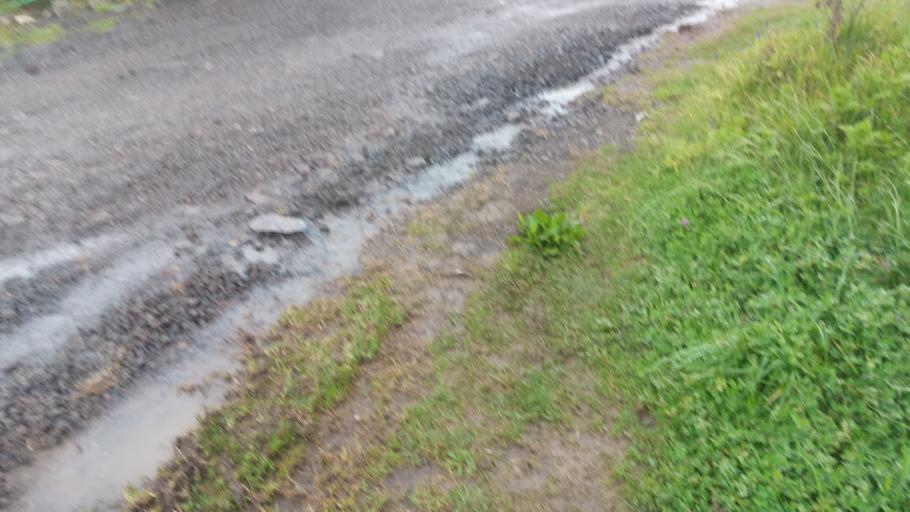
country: ET
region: Oromiya
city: Adis `Alem
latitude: 9.1731
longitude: 38.1278
